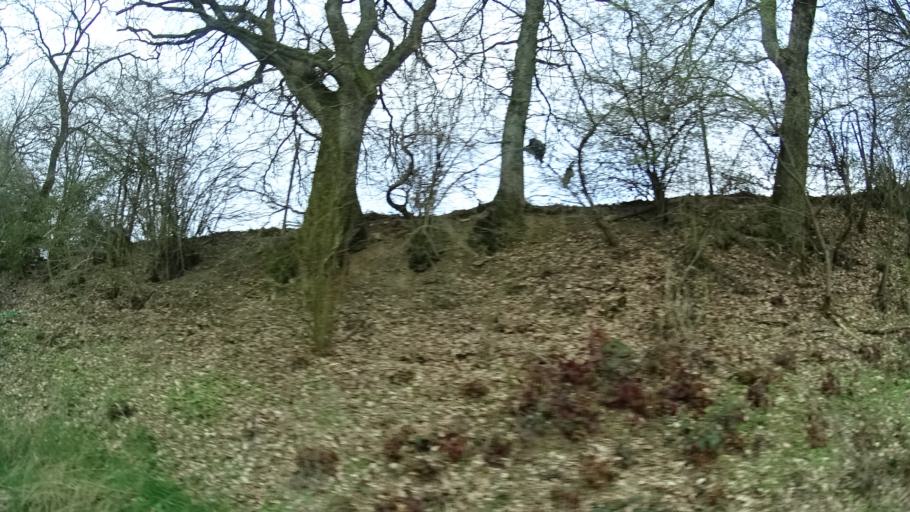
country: DE
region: Rheinland-Pfalz
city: Leisel
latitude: 49.7204
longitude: 7.2022
